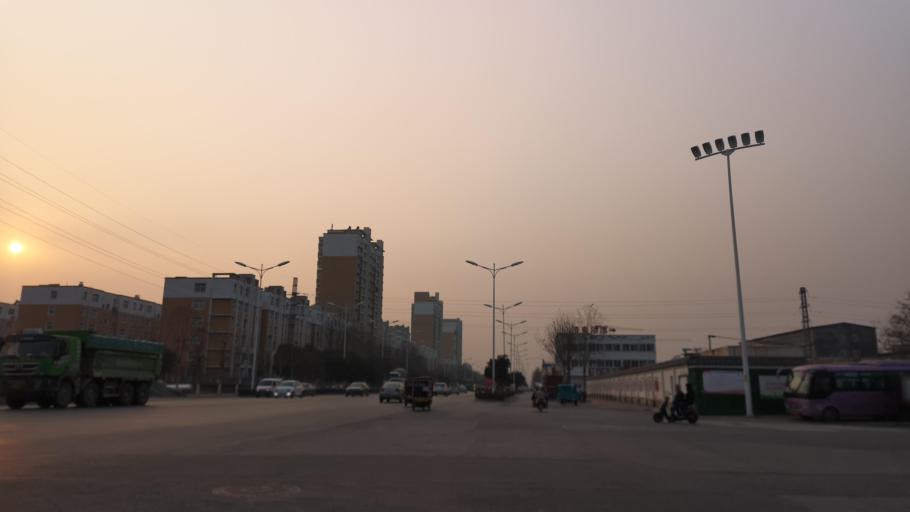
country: CN
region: Henan Sheng
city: Zhongyuanlu
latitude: 35.7891
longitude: 115.0902
